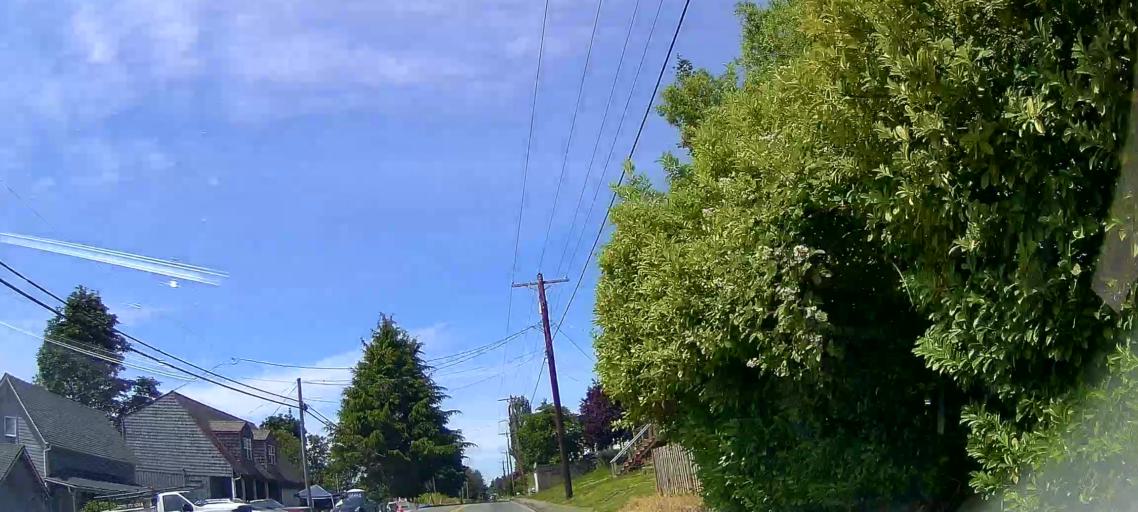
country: US
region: Washington
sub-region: Snohomish County
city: Stanwood
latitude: 48.2449
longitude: -122.3480
